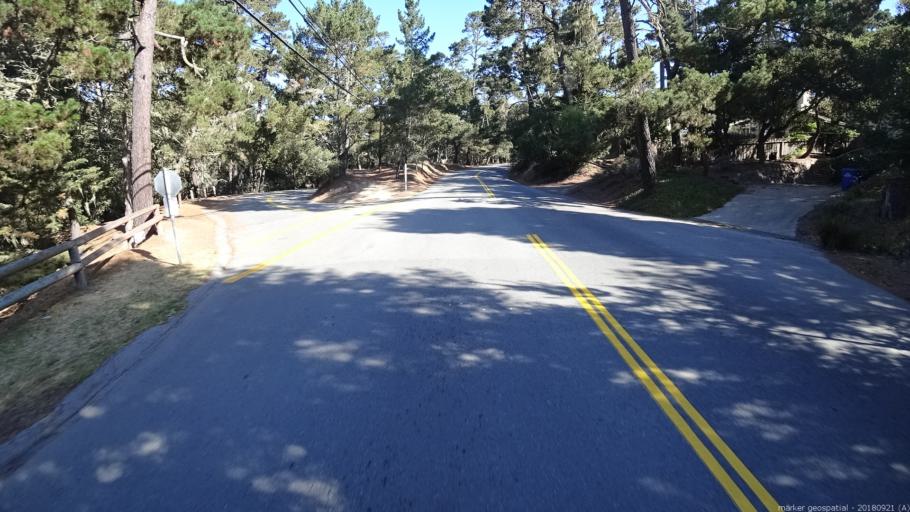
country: US
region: California
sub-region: Monterey County
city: Carmel-by-the-Sea
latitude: 36.5613
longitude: -121.9201
